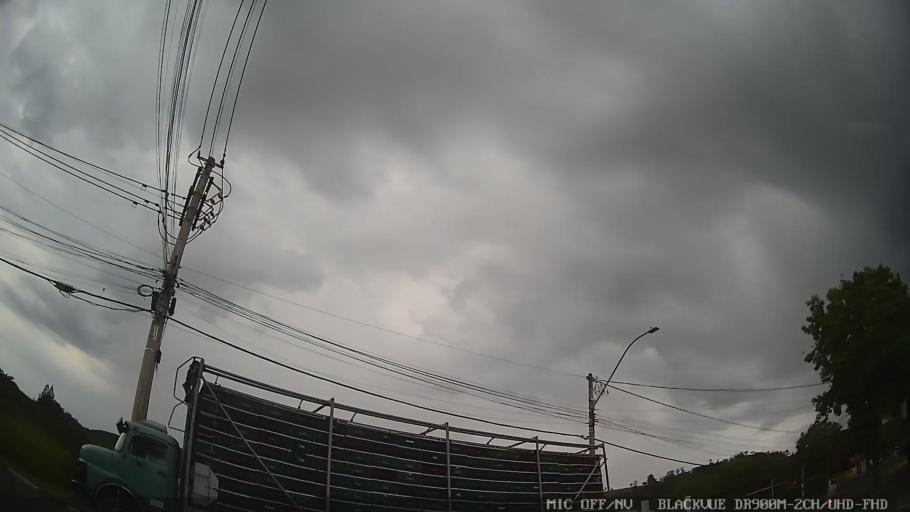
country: BR
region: Sao Paulo
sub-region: Amparo
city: Amparo
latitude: -22.7086
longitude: -46.8134
